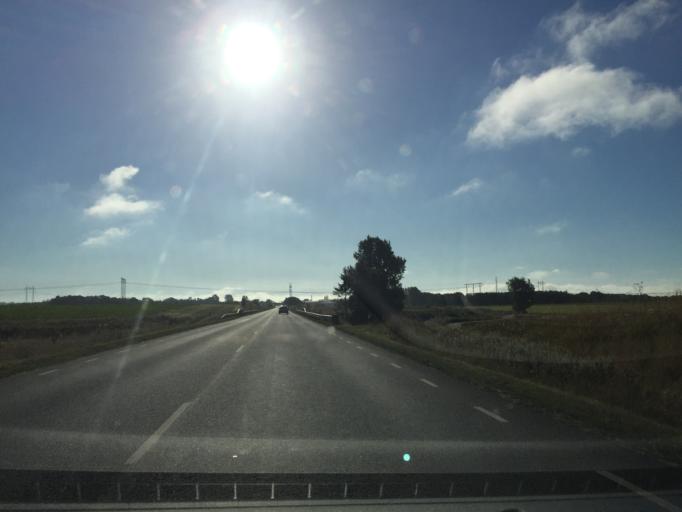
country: SE
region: Skane
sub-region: Staffanstorps Kommun
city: Staffanstorp
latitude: 55.6635
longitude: 13.2074
